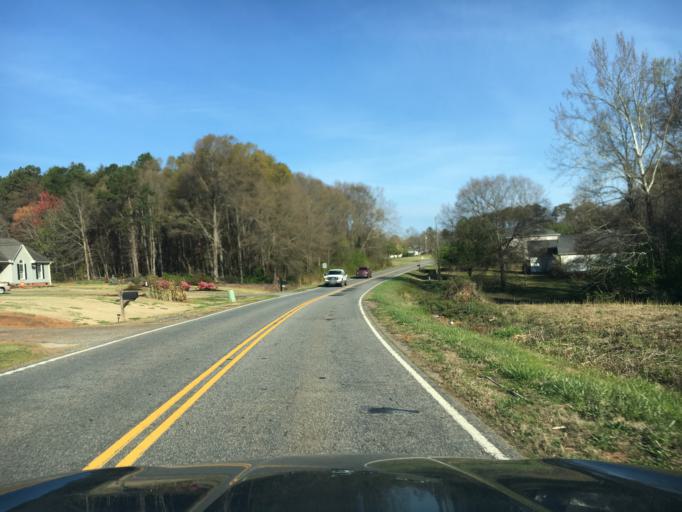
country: US
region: South Carolina
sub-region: Greenville County
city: Greer
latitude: 34.9655
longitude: -82.1928
